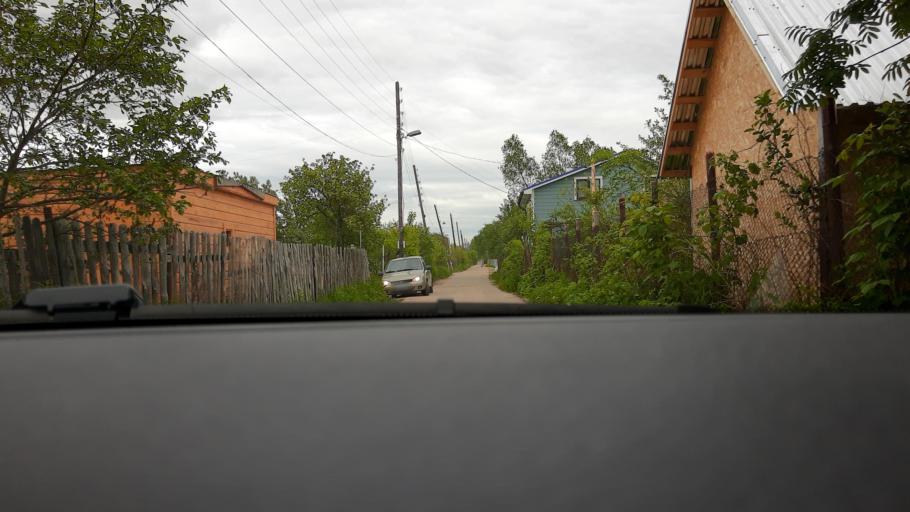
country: RU
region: Nizjnij Novgorod
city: Gorbatovka
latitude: 56.2597
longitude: 43.8298
